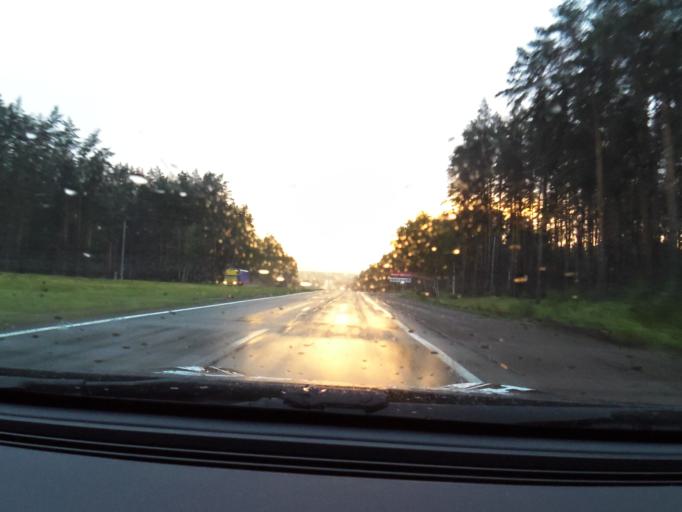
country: RU
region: Tatarstan
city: Mendeleyevsk
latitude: 55.7561
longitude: 52.2377
